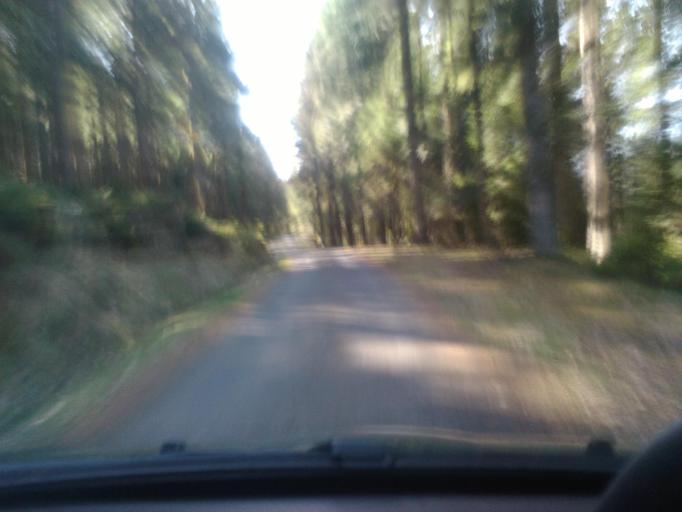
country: FR
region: Lorraine
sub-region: Departement des Vosges
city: Xonrupt-Longemer
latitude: 48.0826
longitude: 6.9529
